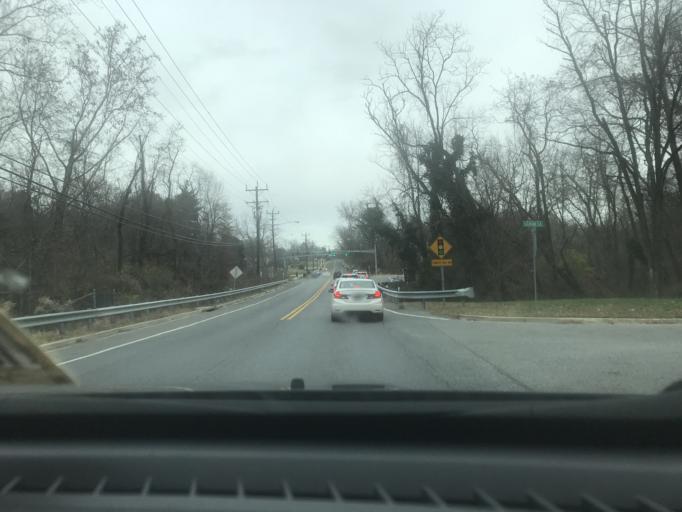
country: US
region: Maryland
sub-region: Prince George's County
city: Temple Hills
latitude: 38.8006
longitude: -76.9305
